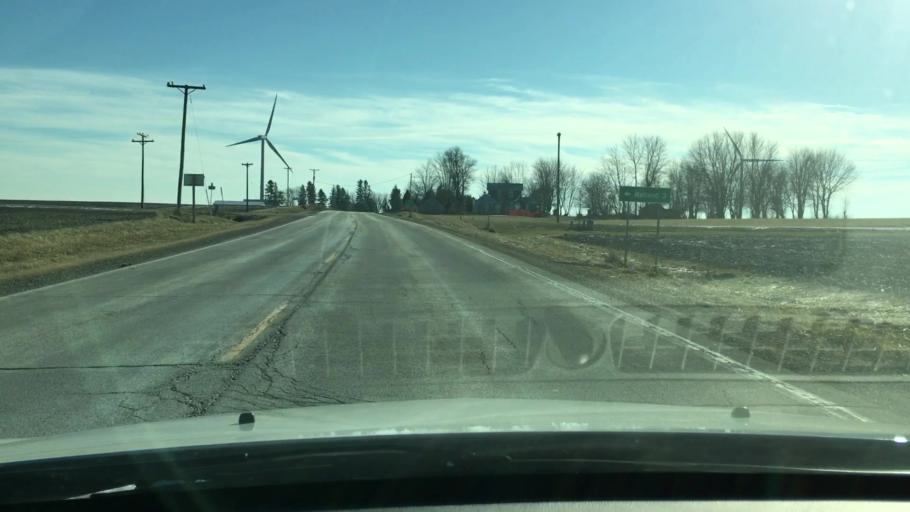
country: US
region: Illinois
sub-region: LaSalle County
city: Mendota
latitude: 41.6287
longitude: -89.1294
